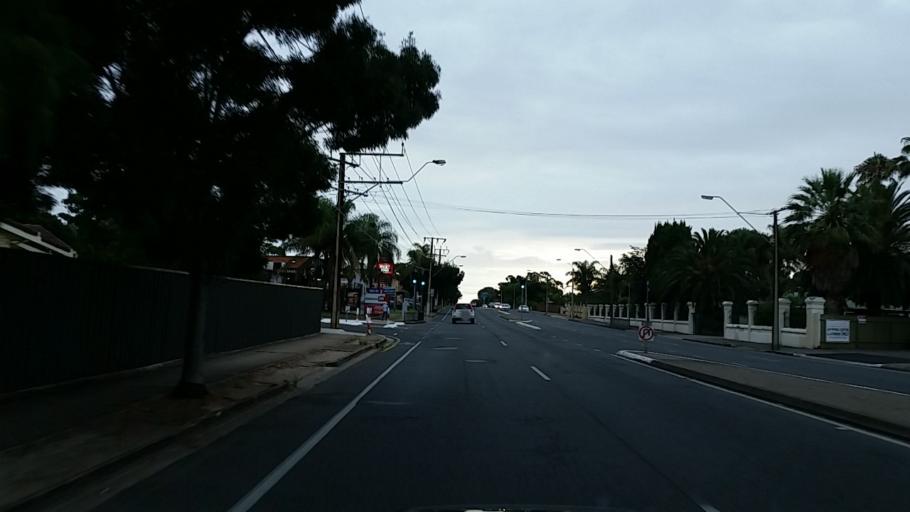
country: AU
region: South Australia
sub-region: Campbelltown
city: Paradise
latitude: -34.8711
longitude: 138.6725
